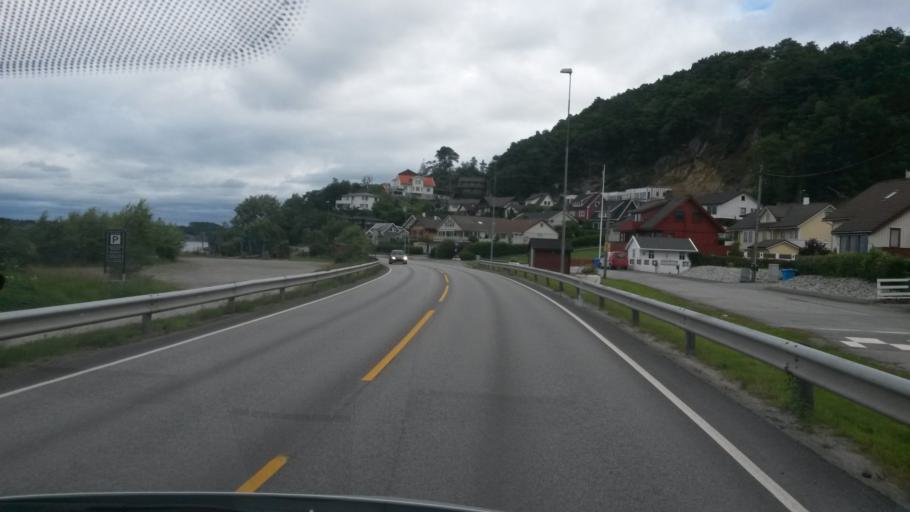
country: NO
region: Rogaland
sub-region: Sandnes
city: Sandnes
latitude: 58.8581
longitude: 5.7550
